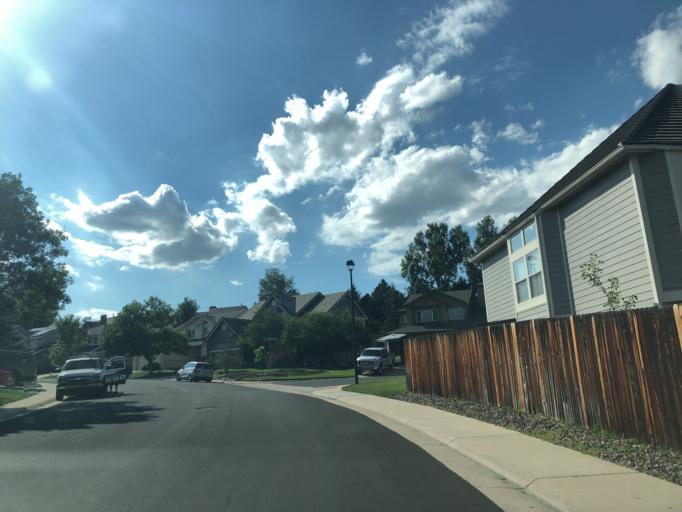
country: US
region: Colorado
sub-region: Arapahoe County
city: Dove Valley
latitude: 39.6117
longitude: -104.7676
